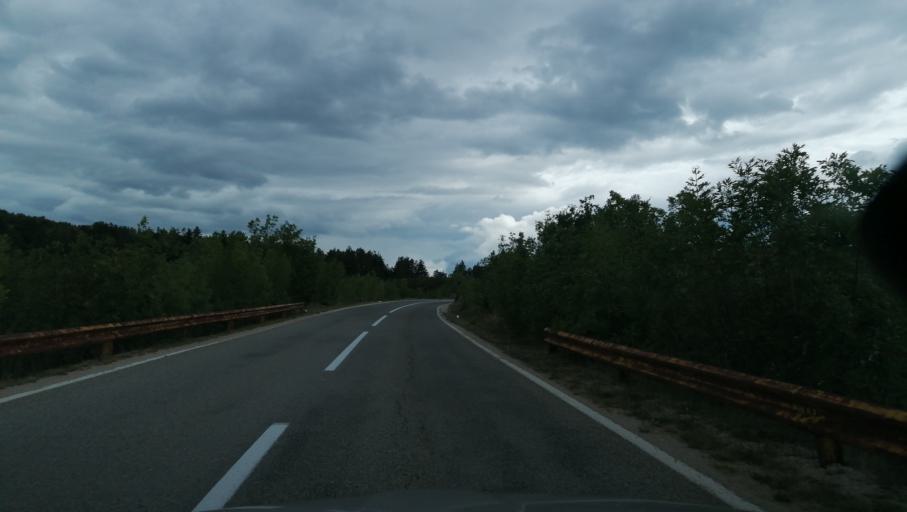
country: BA
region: Republika Srpska
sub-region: Opstina Bileca
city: Bileca
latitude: 43.0191
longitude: 18.4322
